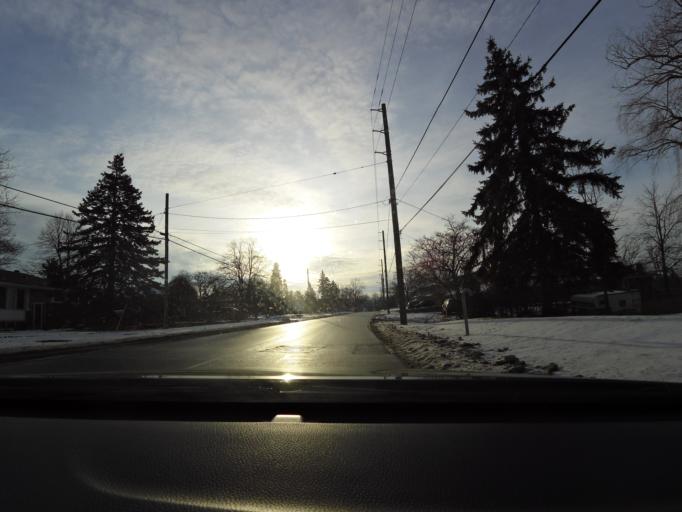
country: CA
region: Ontario
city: Ancaster
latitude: 43.0697
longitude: -79.9405
